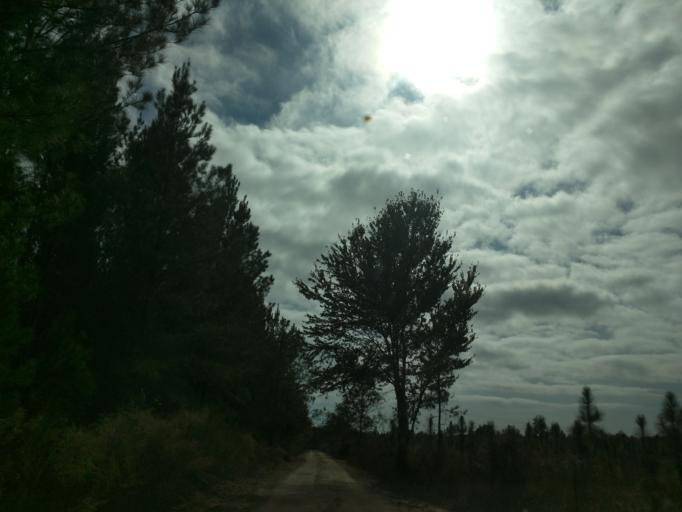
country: US
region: Florida
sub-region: Escambia County
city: Cantonment
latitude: 30.5370
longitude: -87.4368
